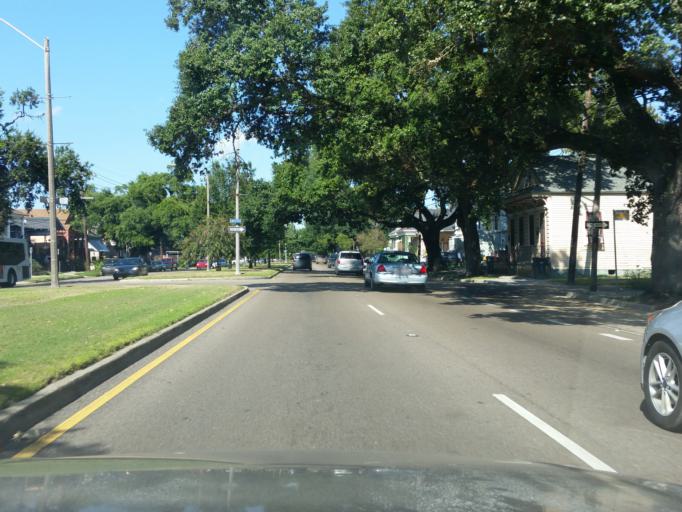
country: US
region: Louisiana
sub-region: Orleans Parish
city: New Orleans
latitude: 29.9790
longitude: -90.0755
